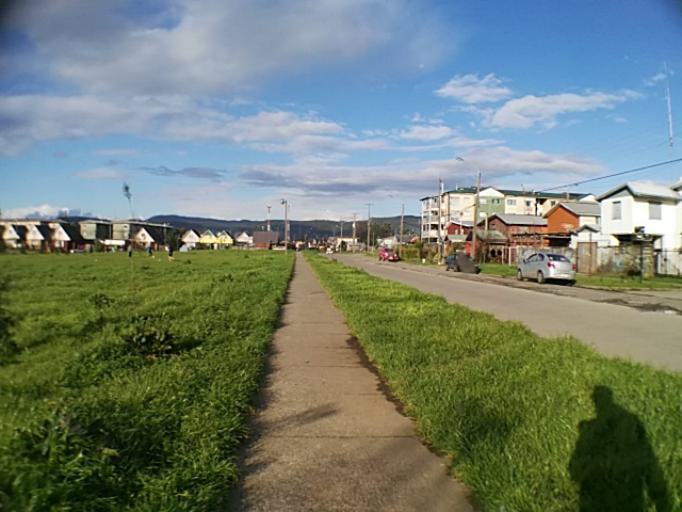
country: CL
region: Los Lagos
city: Las Animas
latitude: -39.8341
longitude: -73.2253
